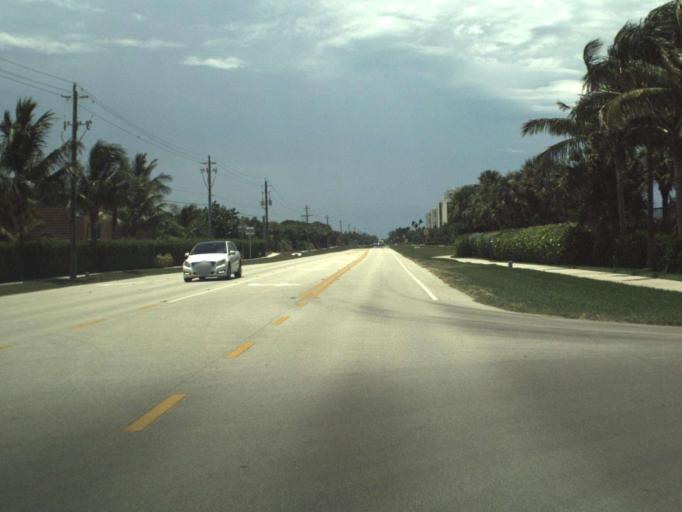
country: US
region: Florida
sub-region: Saint Lucie County
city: Hutchinson Island South
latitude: 27.2938
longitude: -80.2158
